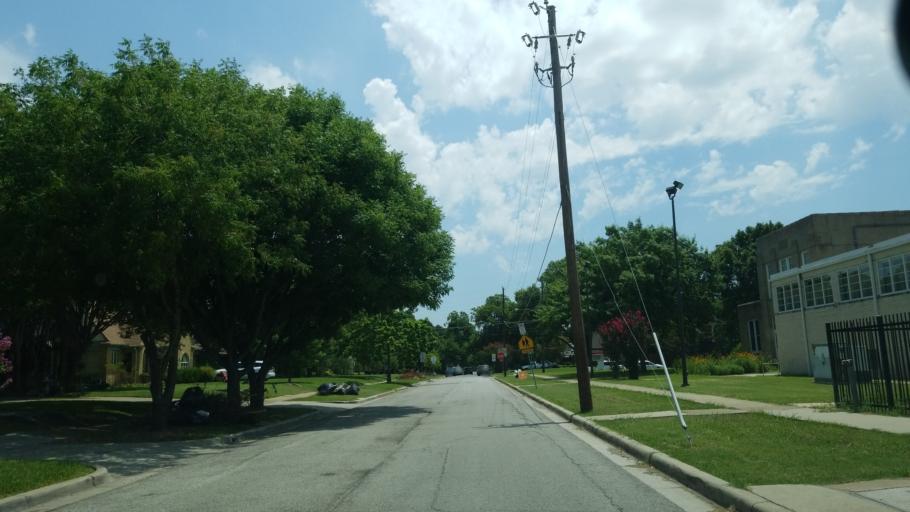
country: US
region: Texas
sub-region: Dallas County
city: Highland Park
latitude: 32.8249
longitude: -96.7669
